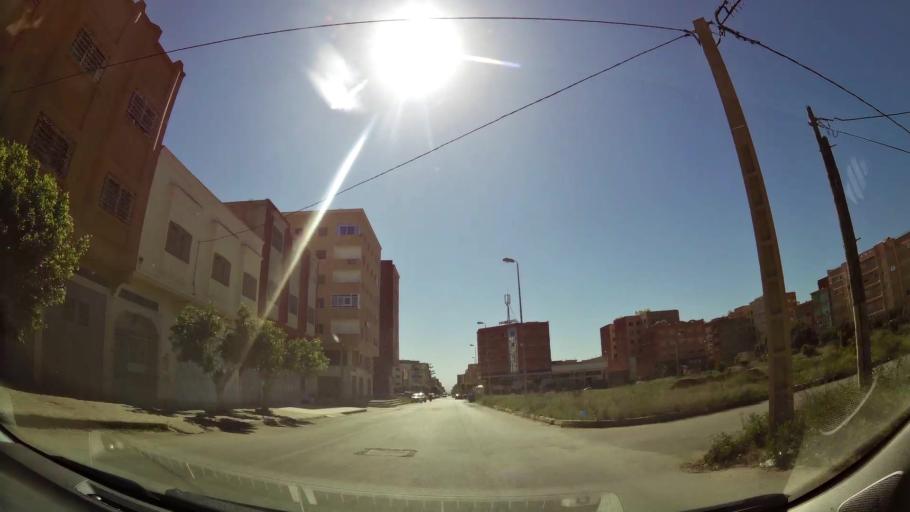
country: MA
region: Oriental
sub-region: Berkane-Taourirt
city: Berkane
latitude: 34.9390
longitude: -2.3302
